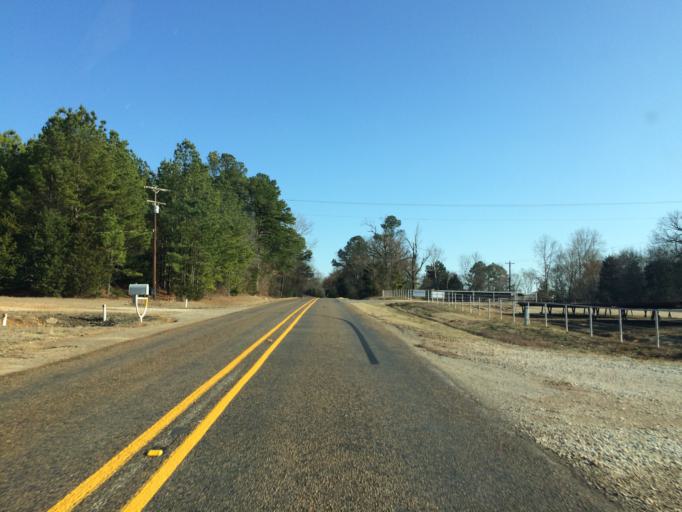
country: US
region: Texas
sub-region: Wood County
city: Quitman
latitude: 32.7057
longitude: -95.3568
